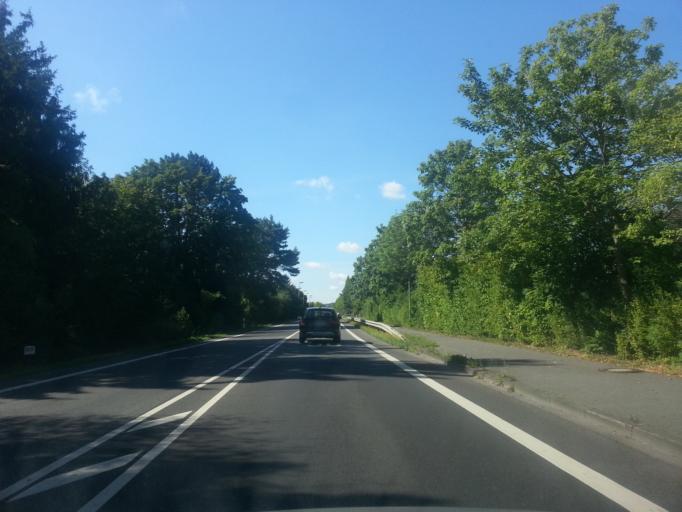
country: DE
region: Hesse
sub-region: Regierungsbezirk Darmstadt
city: Dietzenbach
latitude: 50.0267
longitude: 8.7852
